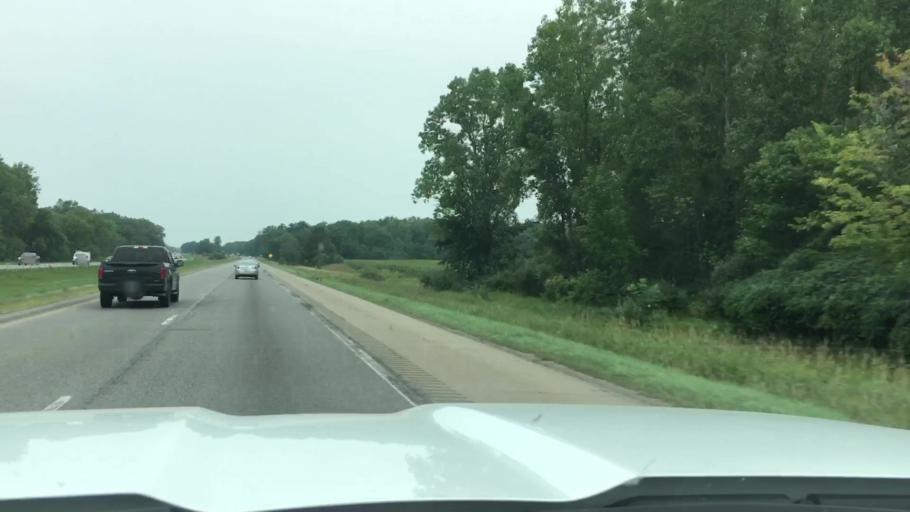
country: US
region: Michigan
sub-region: Ingham County
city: Williamston
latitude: 42.6664
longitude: -84.2372
